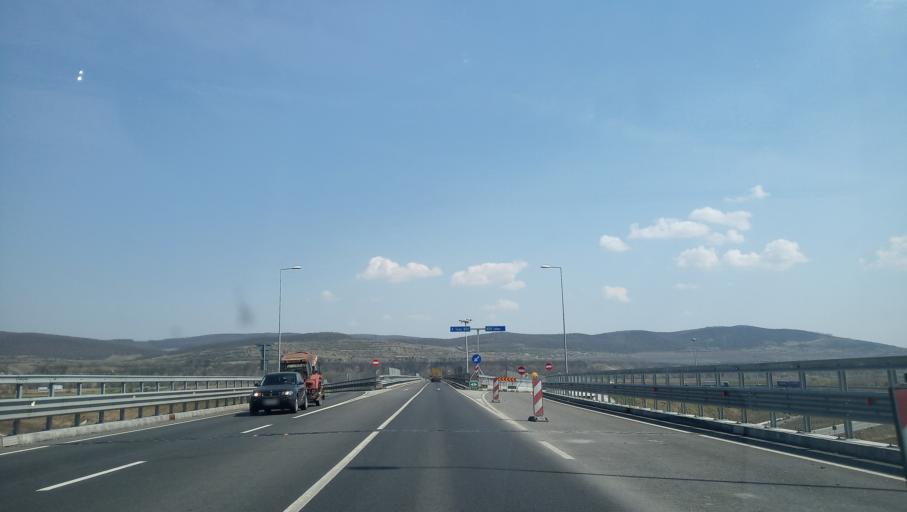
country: RO
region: Alba
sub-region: Municipiul Aiud
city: Aiud
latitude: 46.3292
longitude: 23.7258
